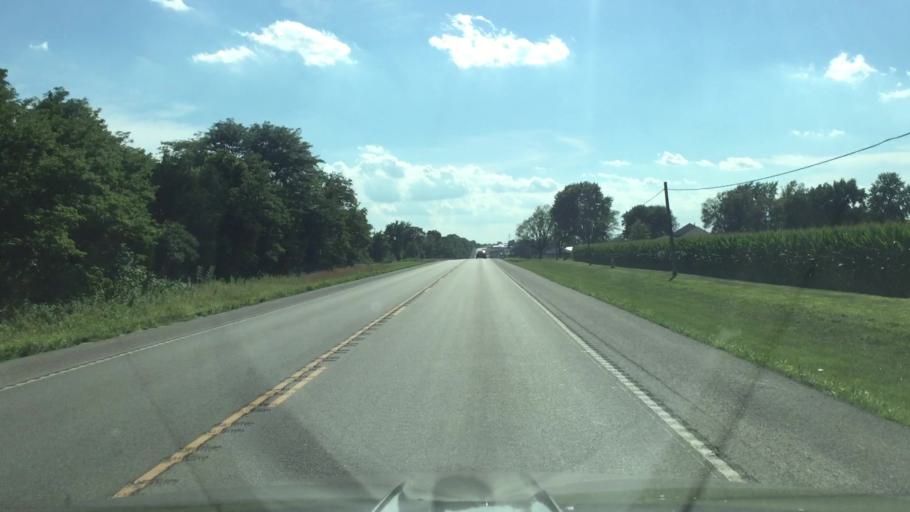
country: US
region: Missouri
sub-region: Morgan County
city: Versailles
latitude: 38.4481
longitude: -92.8022
